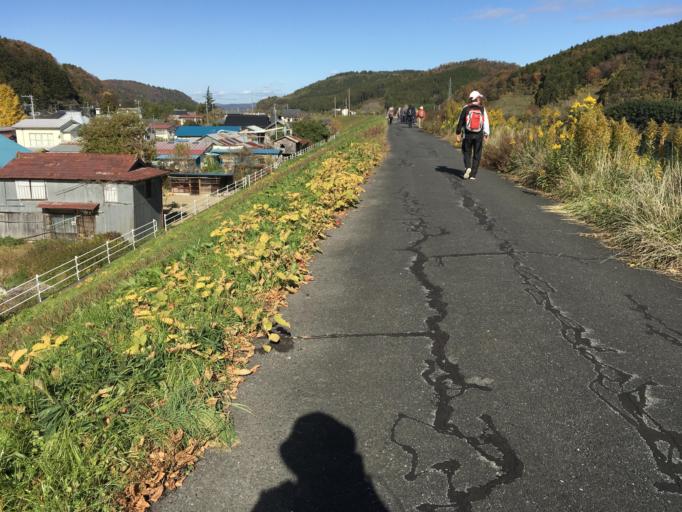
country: JP
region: Miyagi
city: Wakuya
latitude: 38.6569
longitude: 141.2856
